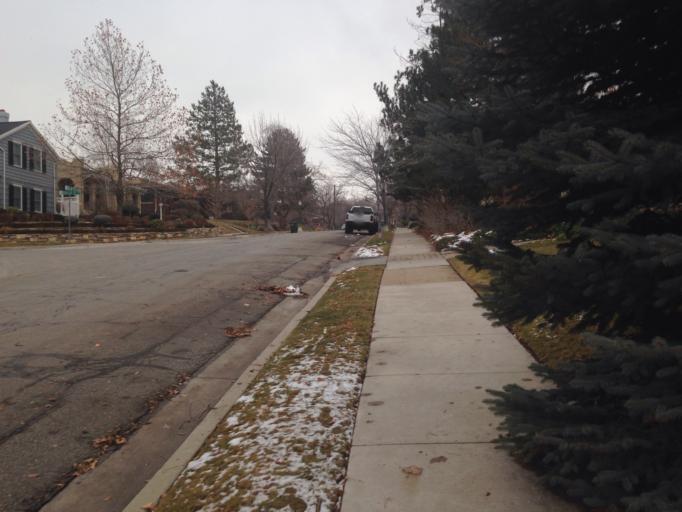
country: US
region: Utah
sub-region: Salt Lake County
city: Salt Lake City
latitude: 40.7458
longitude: -111.8557
